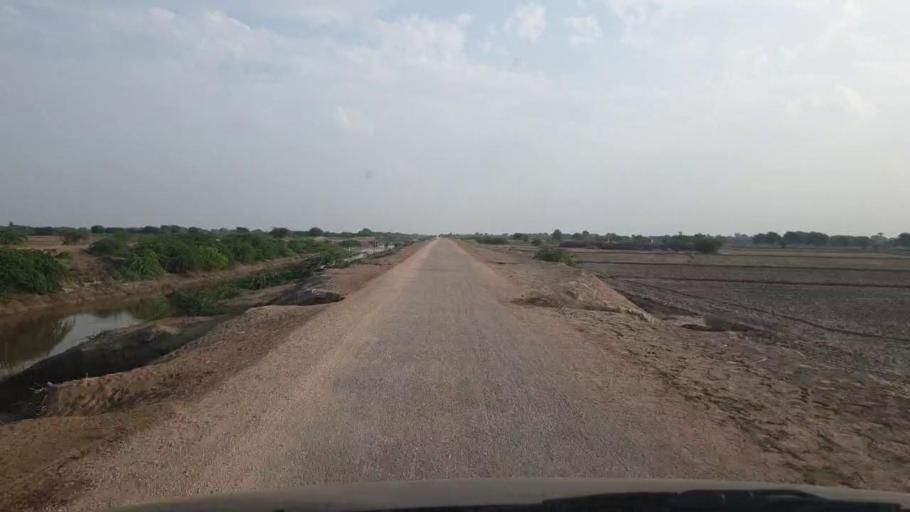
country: PK
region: Sindh
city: Badin
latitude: 24.5421
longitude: 68.6737
